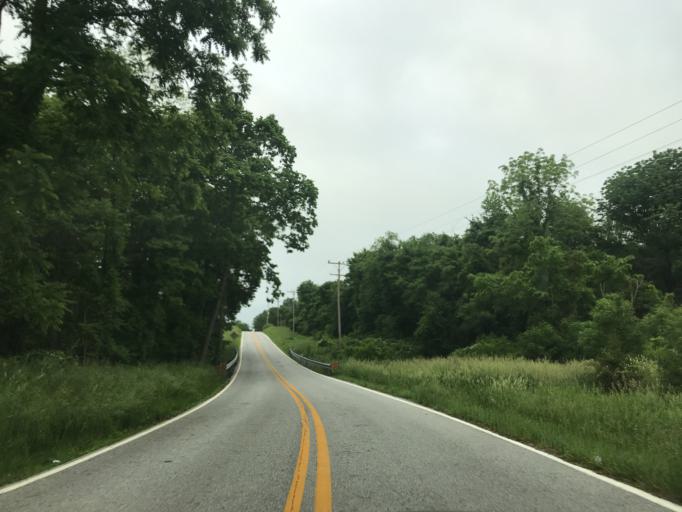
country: US
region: Maryland
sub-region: Frederick County
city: Emmitsburg
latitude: 39.6879
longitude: -77.3305
